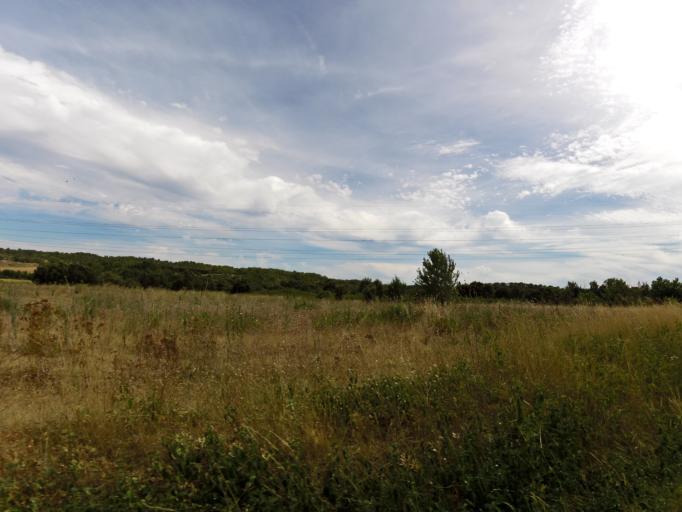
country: FR
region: Languedoc-Roussillon
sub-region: Departement du Gard
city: Saint-Mamert-du-Gard
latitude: 43.8770
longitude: 4.1778
